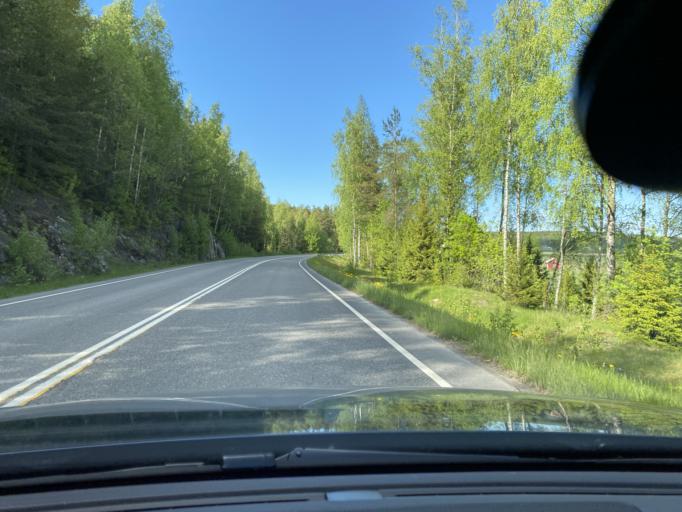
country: FI
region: Varsinais-Suomi
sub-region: Turku
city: Sauvo
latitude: 60.3604
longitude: 22.6715
